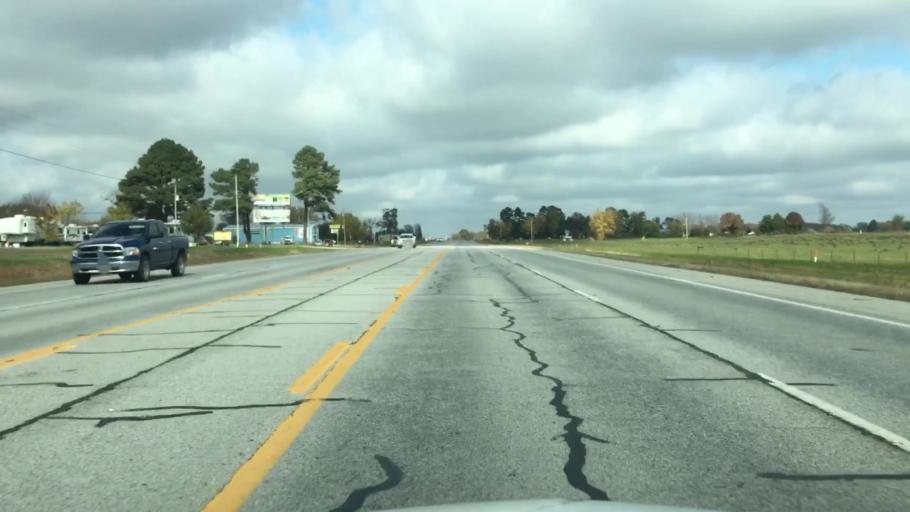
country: US
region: Arkansas
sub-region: Benton County
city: Gentry
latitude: 36.2208
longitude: -94.4953
